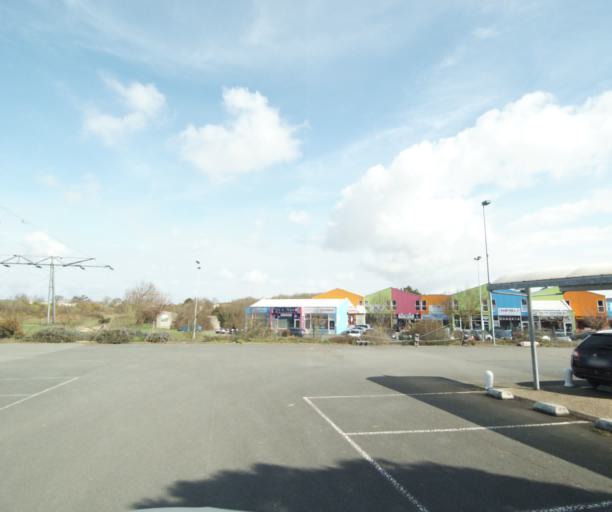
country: FR
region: Poitou-Charentes
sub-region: Departement de la Charente-Maritime
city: Lagord
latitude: 46.1750
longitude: -1.1674
